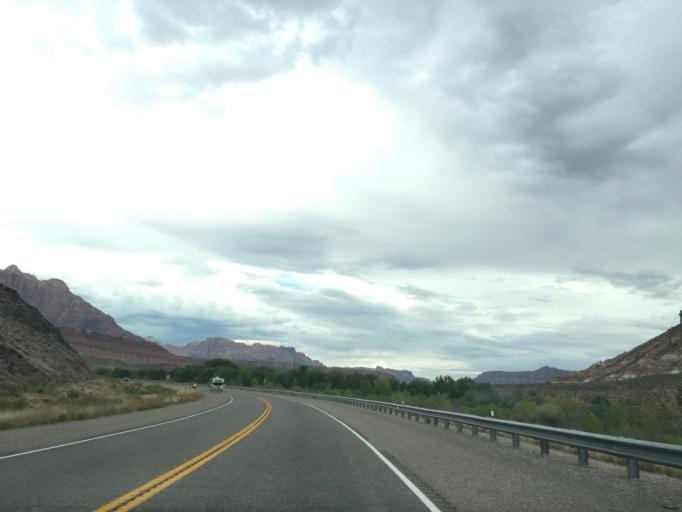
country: US
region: Utah
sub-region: Washington County
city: LaVerkin
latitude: 37.1681
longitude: -113.1015
